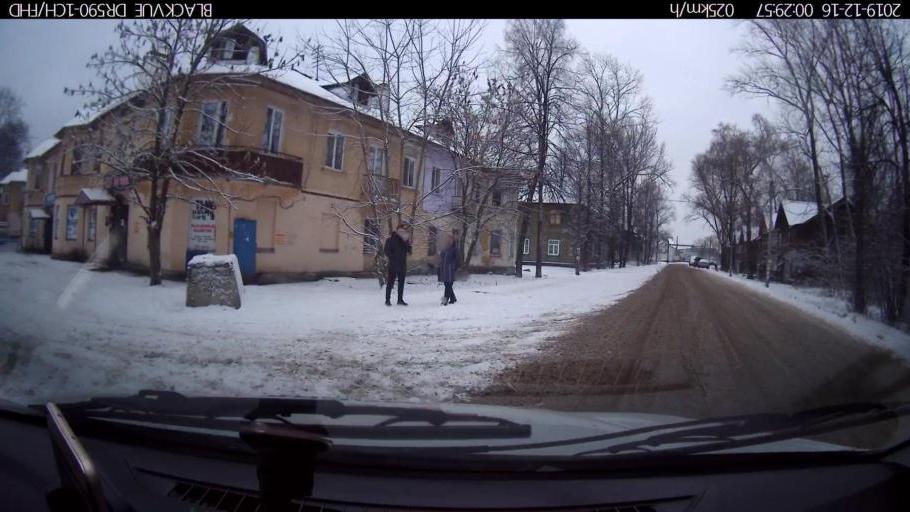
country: RU
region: Nizjnij Novgorod
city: Nizhniy Novgorod
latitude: 56.3099
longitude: 43.8906
